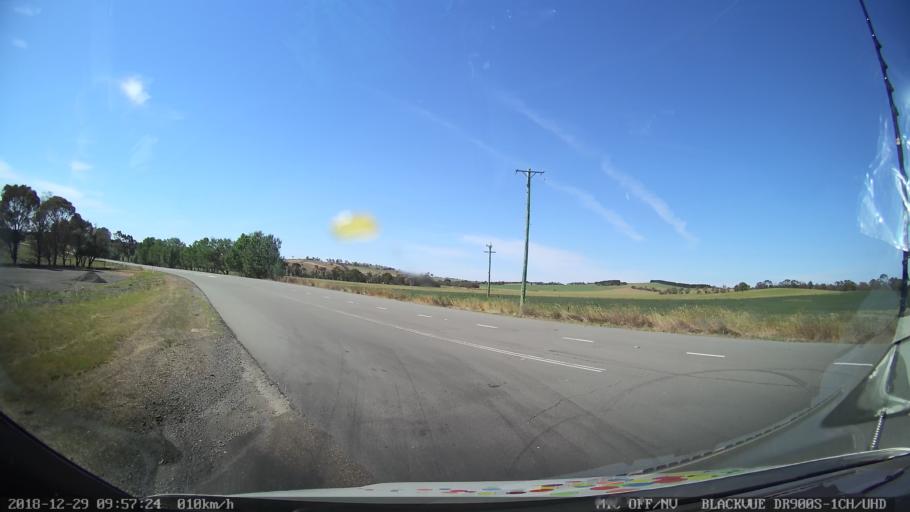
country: AU
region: New South Wales
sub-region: Goulburn Mulwaree
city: Goulburn
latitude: -34.7860
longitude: 149.4807
